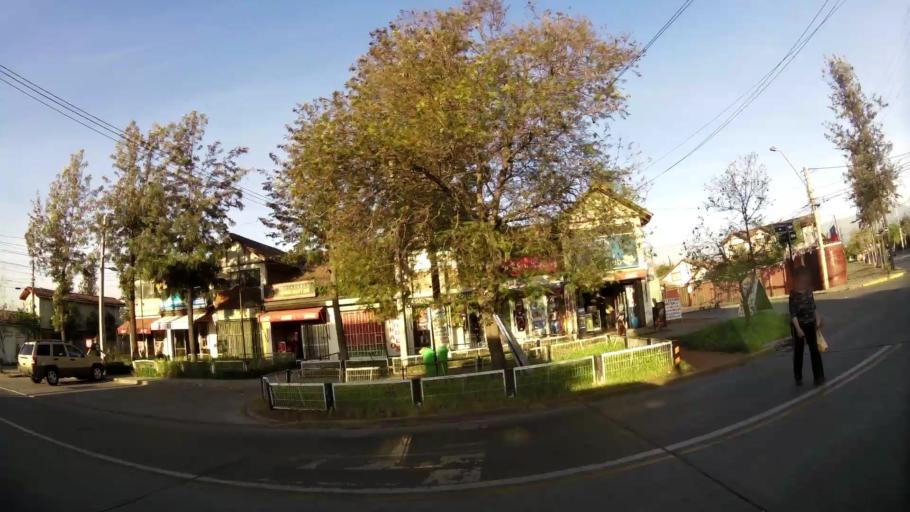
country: CL
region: Santiago Metropolitan
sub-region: Provincia de Santiago
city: La Pintana
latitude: -33.5517
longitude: -70.5829
